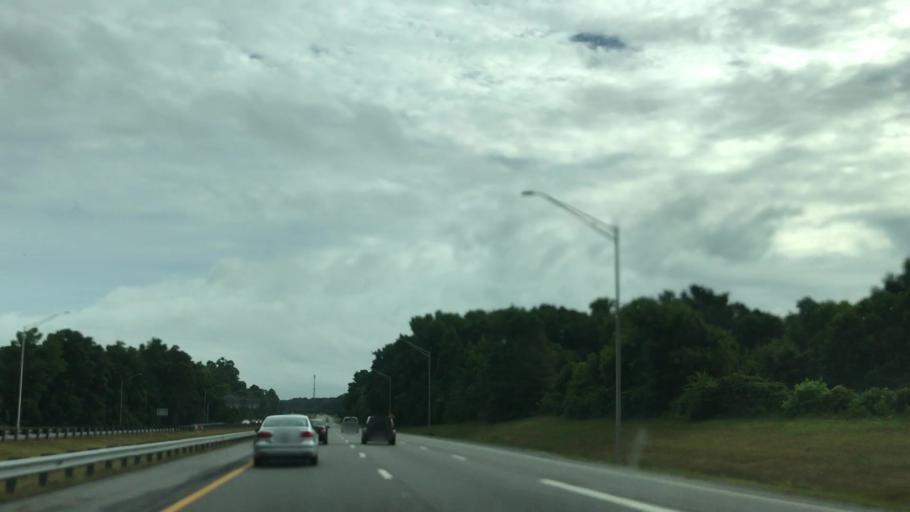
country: US
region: North Carolina
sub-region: Nash County
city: Red Oak
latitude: 36.0659
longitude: -77.8206
